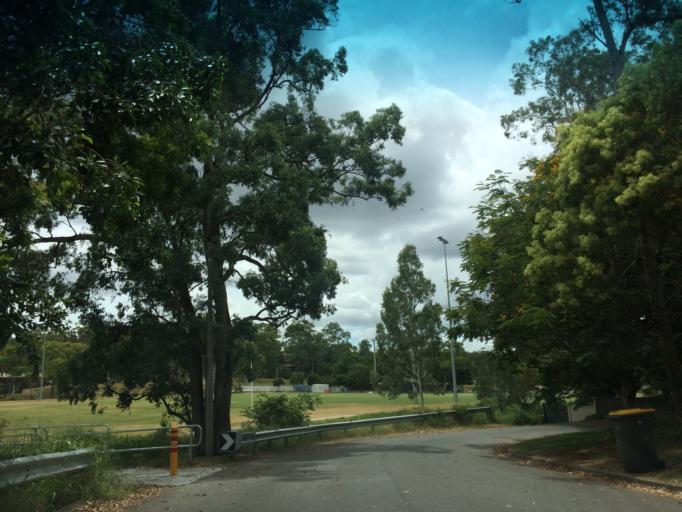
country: AU
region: Queensland
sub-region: Brisbane
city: Kenmore Hills
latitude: -27.5160
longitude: 152.9521
